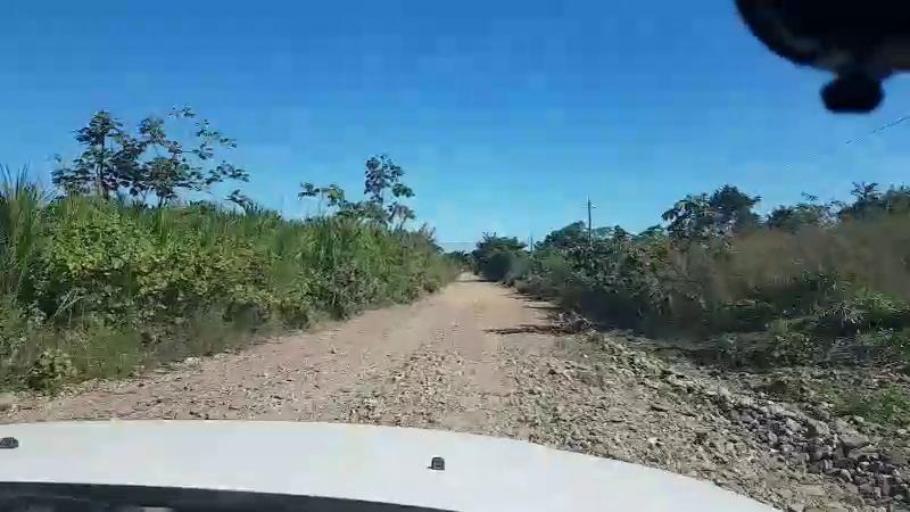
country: BZ
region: Stann Creek
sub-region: Dangriga
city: Dangriga
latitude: 17.1581
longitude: -88.3319
